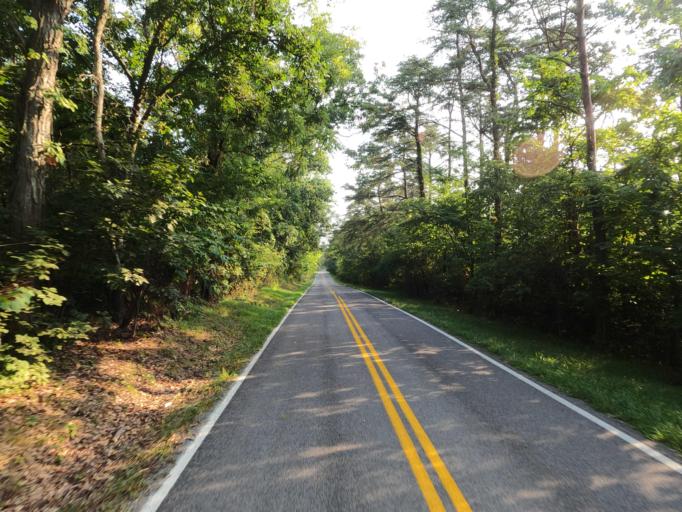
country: US
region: West Virginia
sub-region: Morgan County
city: Berkeley Springs
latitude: 39.6622
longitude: -78.2864
